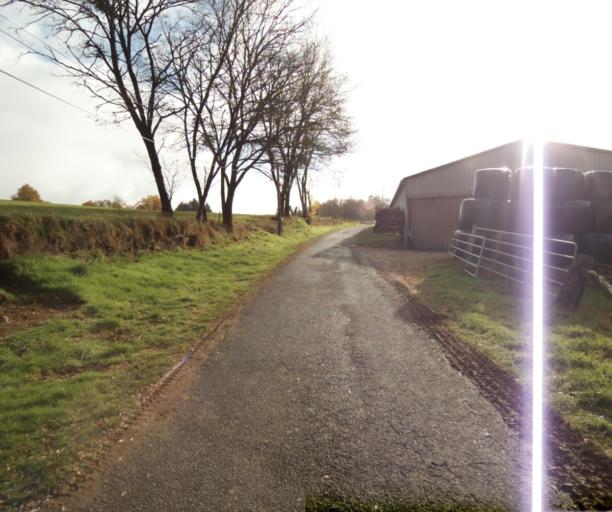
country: FR
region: Limousin
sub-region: Departement de la Correze
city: Cornil
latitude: 45.2032
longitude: 1.6373
